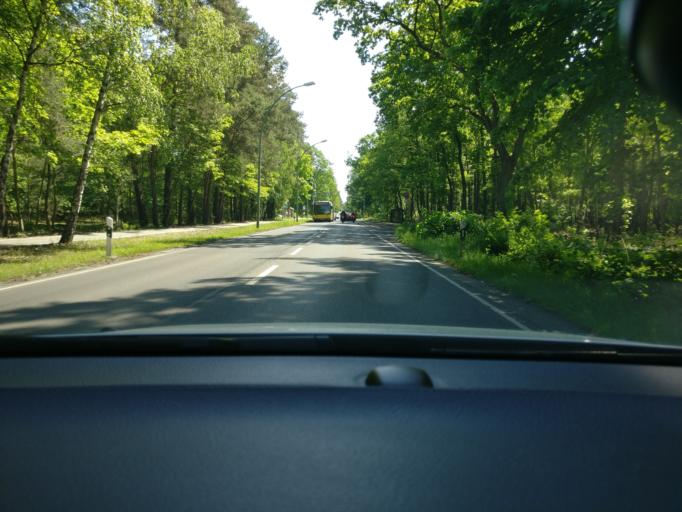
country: DE
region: Berlin
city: Friedrichshagen
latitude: 52.4243
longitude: 13.6274
